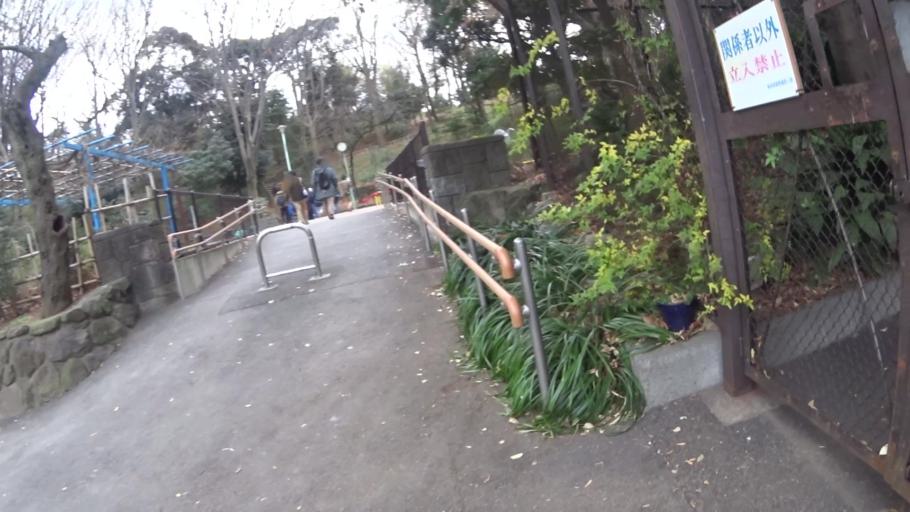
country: JP
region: Kanagawa
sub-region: Kawasaki-shi
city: Kawasaki
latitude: 35.5806
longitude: 139.7072
